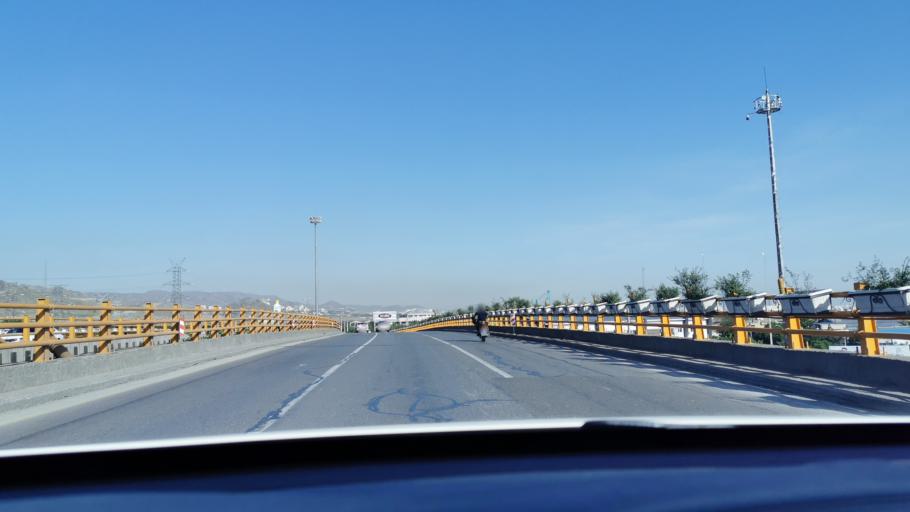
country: IR
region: Razavi Khorasan
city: Mashhad
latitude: 36.2557
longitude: 59.5994
